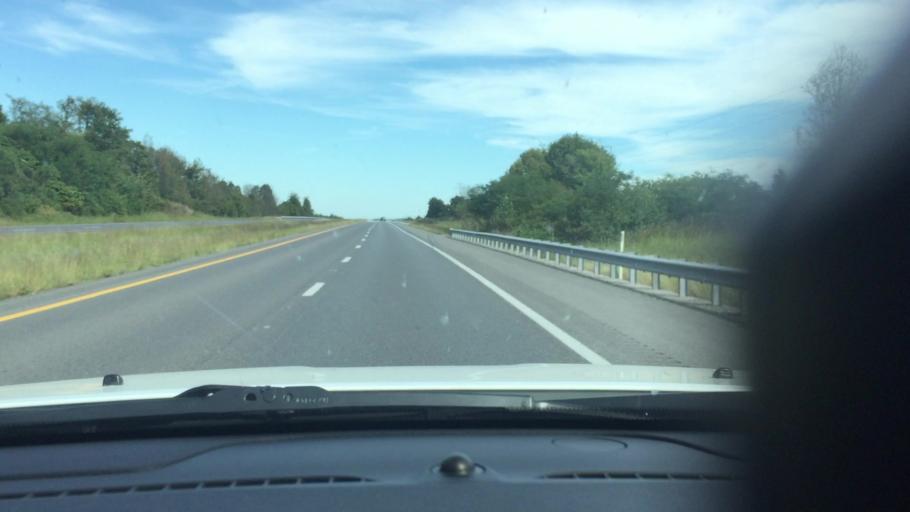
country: US
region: Kentucky
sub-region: Caldwell County
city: Princeton
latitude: 37.1101
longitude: -87.9489
